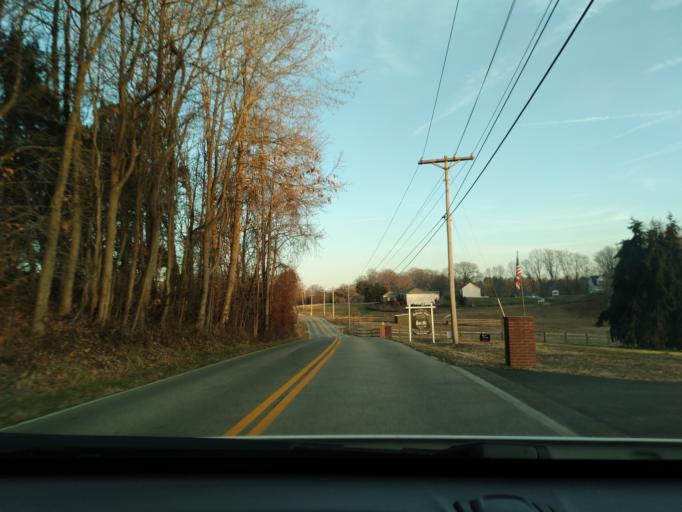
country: US
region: Maryland
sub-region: Calvert County
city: Prince Frederick
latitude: 38.5884
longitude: -76.5507
